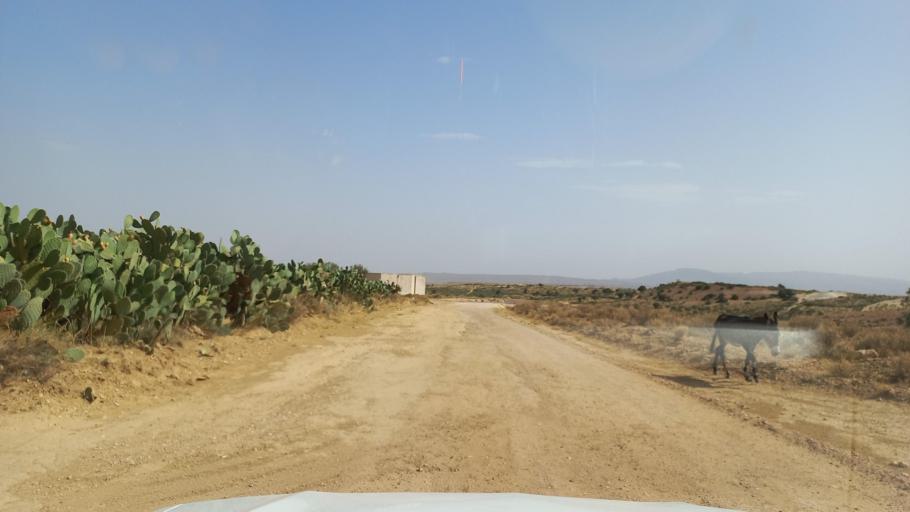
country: TN
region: Al Qasrayn
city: Kasserine
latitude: 35.3055
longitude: 8.9401
